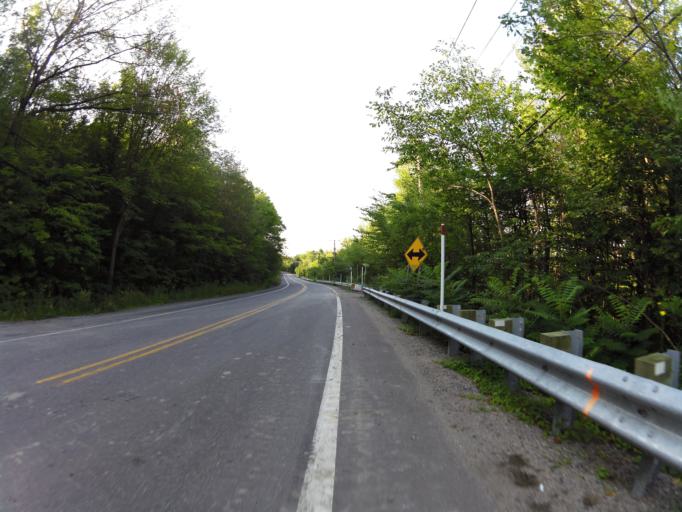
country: CA
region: Quebec
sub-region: Outaouais
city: Wakefield
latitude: 45.5473
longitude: -75.8210
